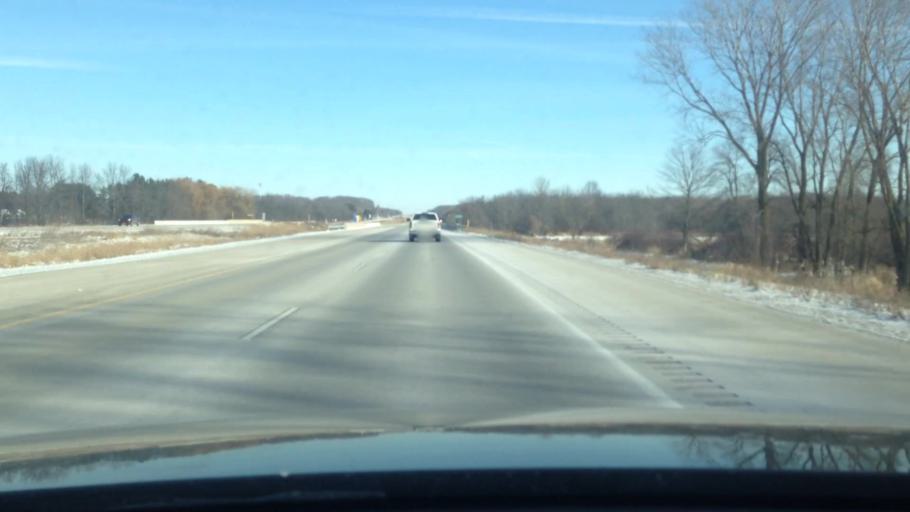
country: US
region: Wisconsin
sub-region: Waukesha County
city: Mukwonago
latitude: 42.8663
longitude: -88.2978
